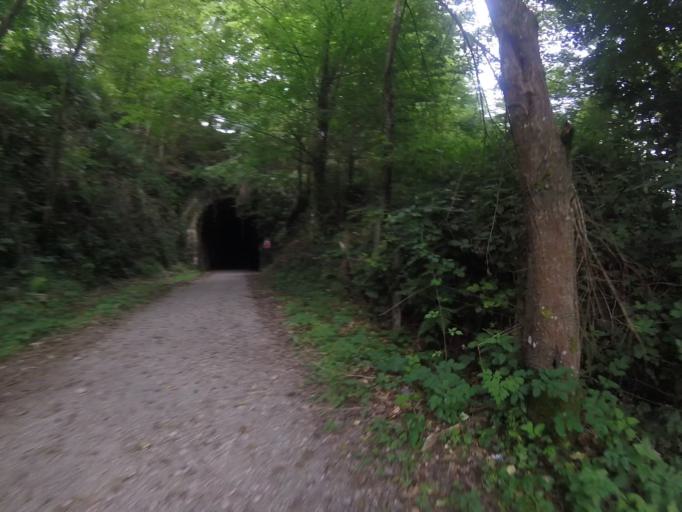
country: ES
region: Navarre
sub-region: Provincia de Navarra
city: Leitza
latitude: 43.0848
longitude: -1.9021
